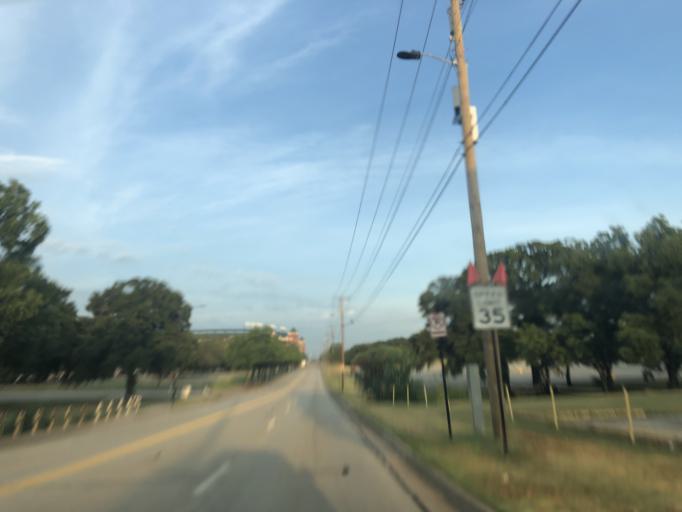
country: US
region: Texas
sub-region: Tarrant County
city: Arlington
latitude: 32.7525
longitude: -97.0754
